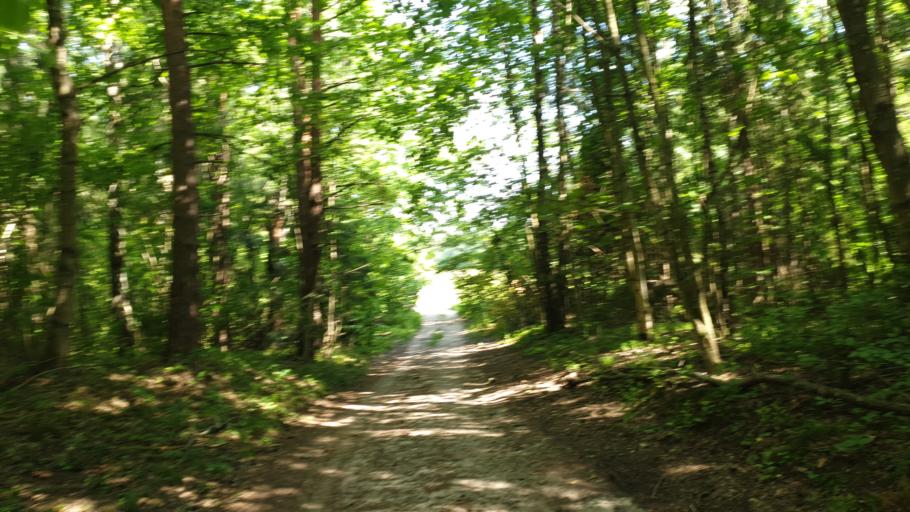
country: LT
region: Vilnius County
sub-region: Vilnius
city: Fabijoniskes
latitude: 54.7885
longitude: 25.3150
